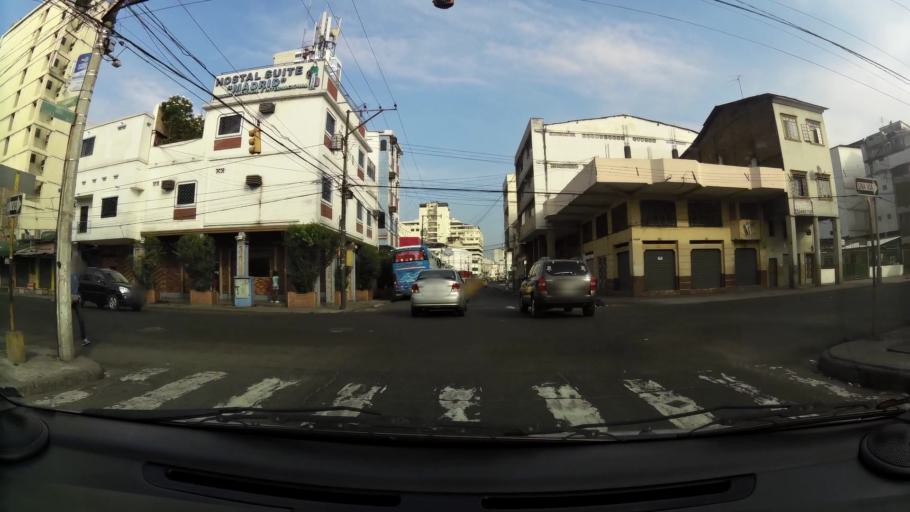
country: EC
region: Guayas
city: Guayaquil
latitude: -2.1886
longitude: -79.8858
